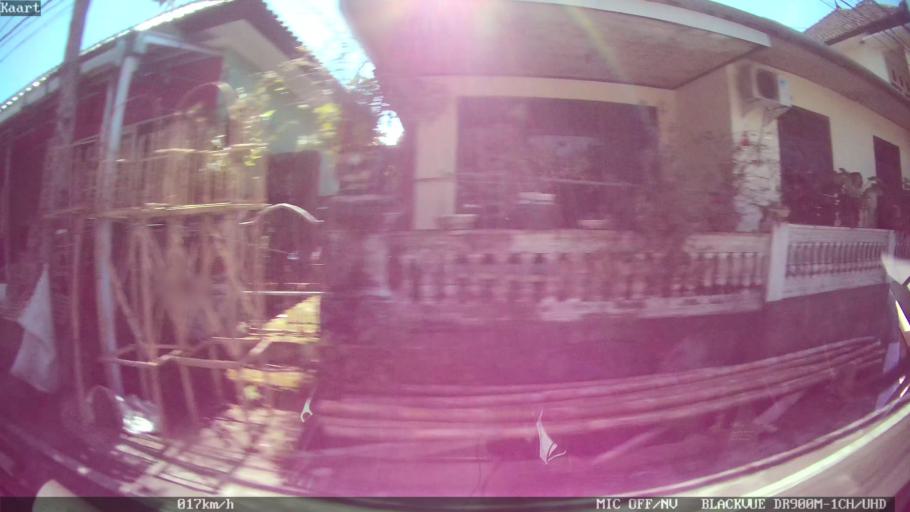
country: ID
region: Bali
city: Banjar Pasekan
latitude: -8.5723
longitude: 115.3297
